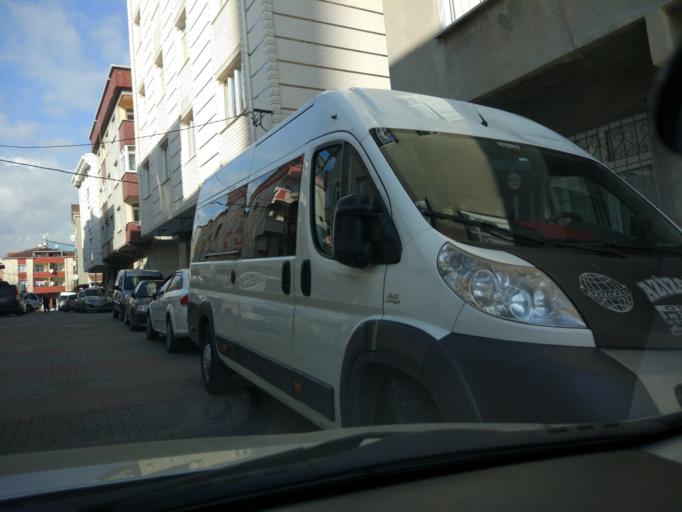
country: TR
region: Istanbul
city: Bahcelievler
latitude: 41.0119
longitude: 28.8313
